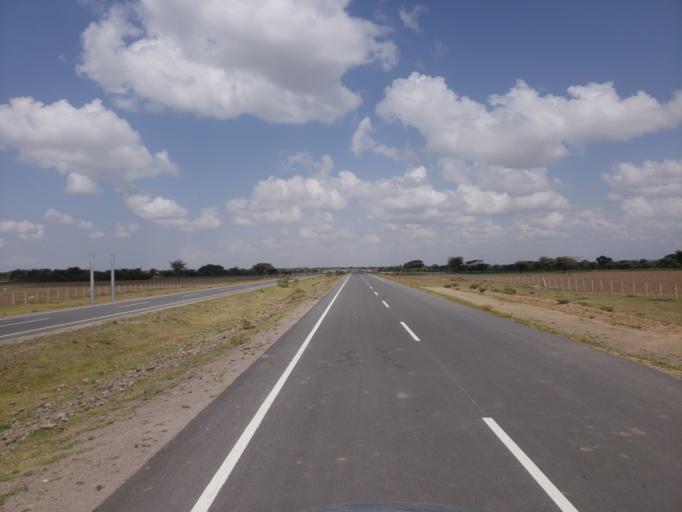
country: ET
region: Oromiya
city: Mojo
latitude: 8.2980
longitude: 38.9316
